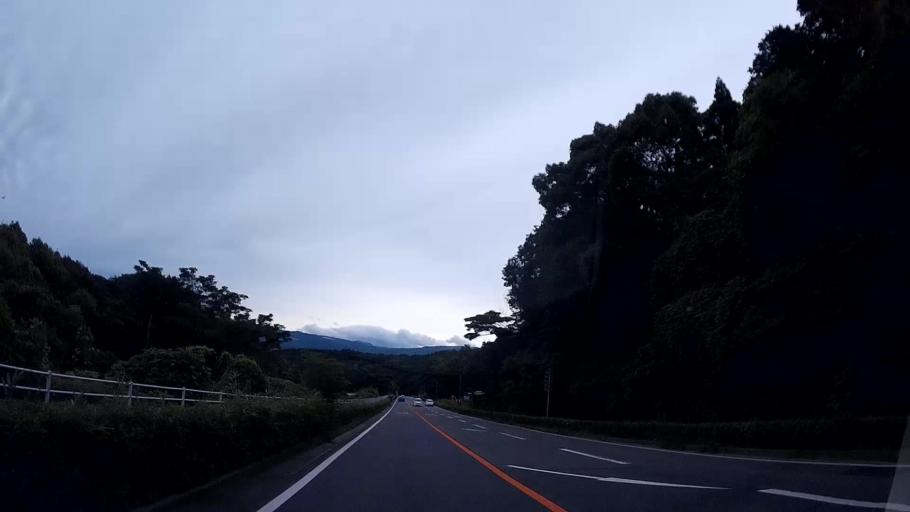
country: JP
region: Kumamoto
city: Ozu
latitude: 32.8447
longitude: 130.8562
